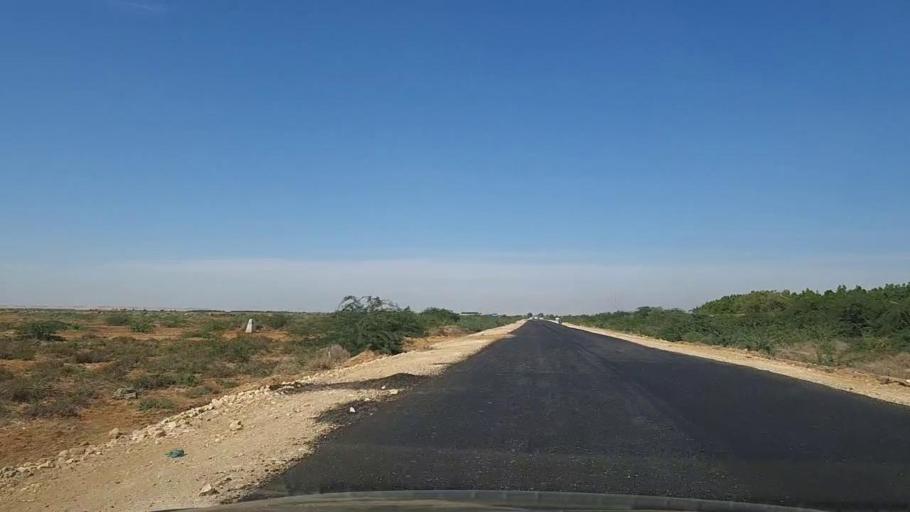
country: PK
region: Sindh
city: Kotri
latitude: 25.2368
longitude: 68.2325
